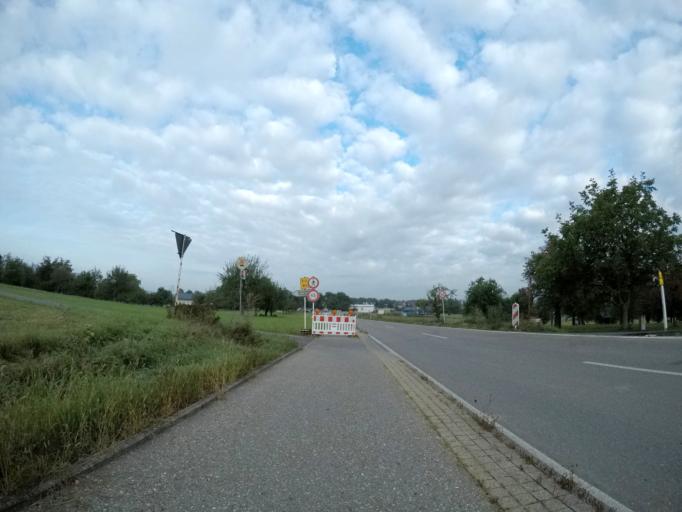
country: DE
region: Baden-Wuerttemberg
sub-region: Tuebingen Region
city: Sickenhausen
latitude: 48.5163
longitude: 9.1868
